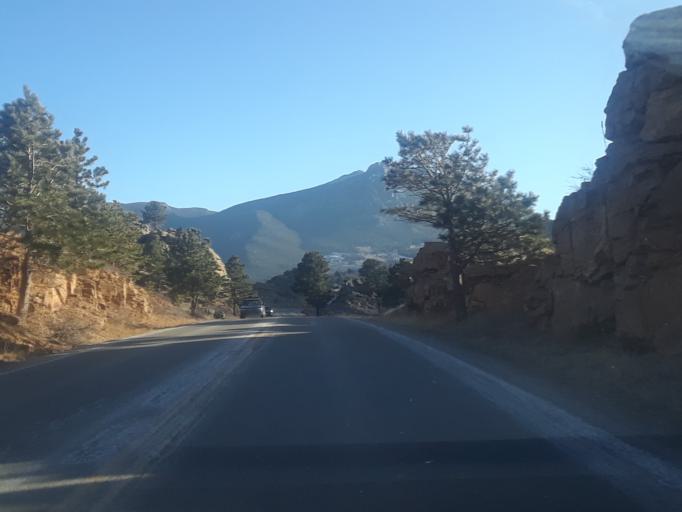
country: US
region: Colorado
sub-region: Larimer County
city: Estes Park
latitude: 40.3450
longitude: -105.5301
